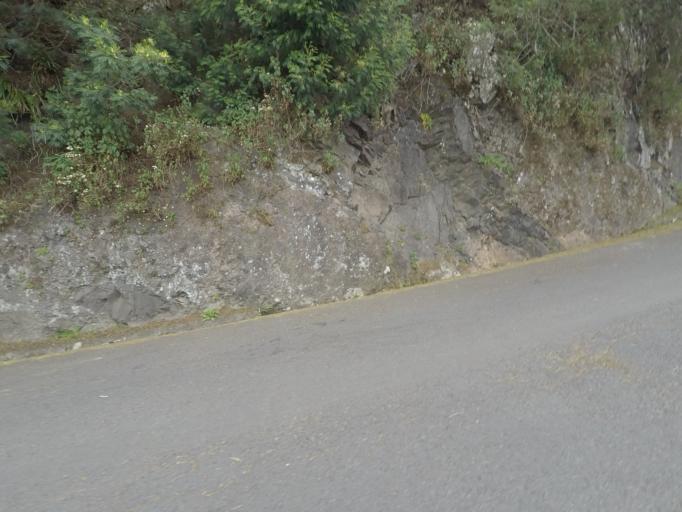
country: PT
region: Madeira
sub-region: Santana
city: Santana
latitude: 32.7931
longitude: -16.8629
